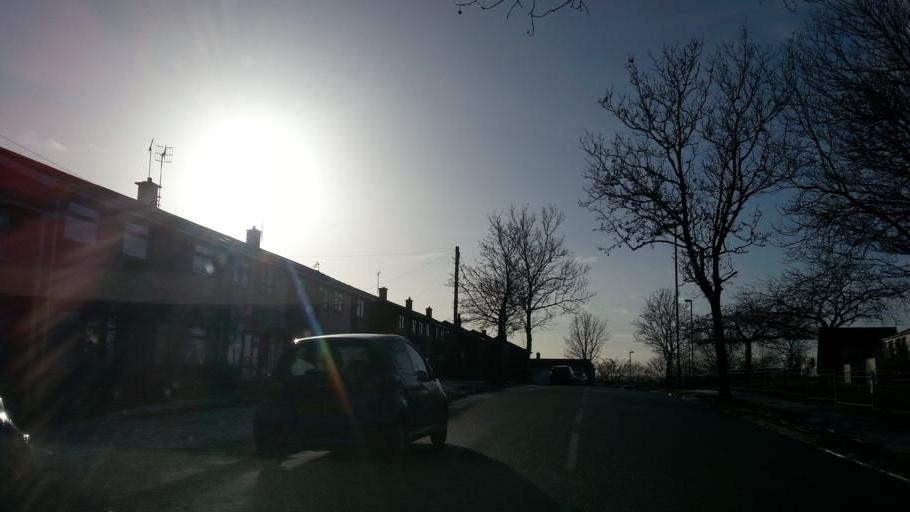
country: GB
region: England
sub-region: Staffordshire
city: Longton
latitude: 52.9864
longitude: -2.1470
